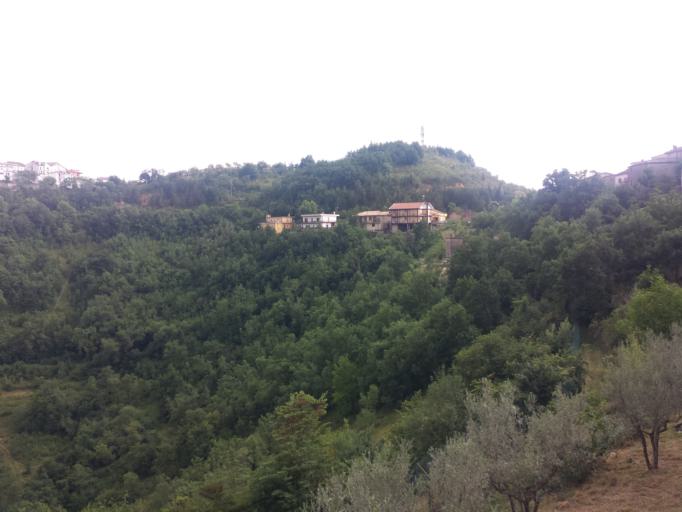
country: IT
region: Latium
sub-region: Provincia di Frosinone
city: Campoli Appennino
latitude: 41.7366
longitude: 13.6780
